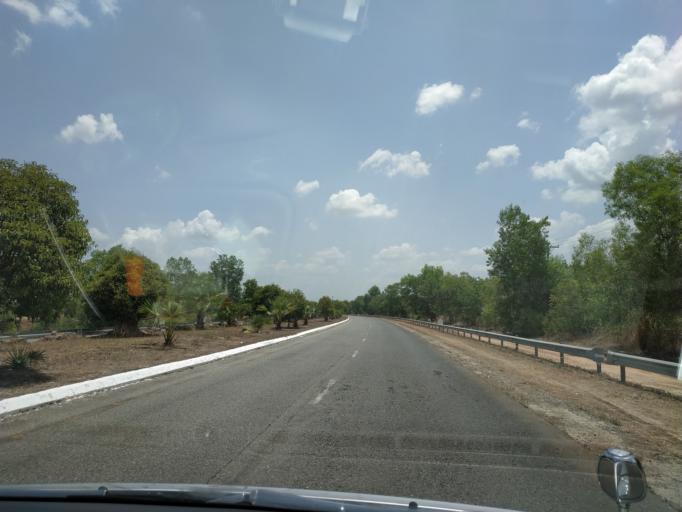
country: MM
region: Bago
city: Thanatpin
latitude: 17.1628
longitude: 96.1971
